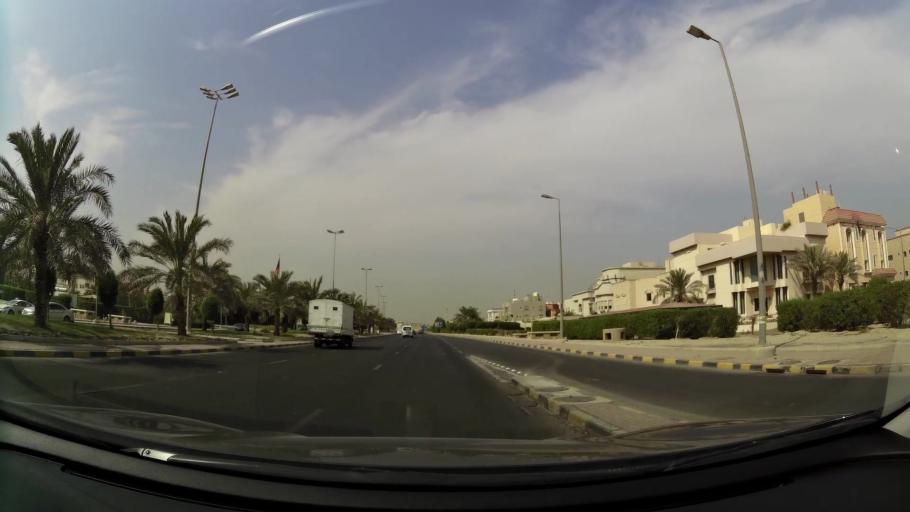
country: KW
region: Al Farwaniyah
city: Janub as Surrah
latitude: 29.2826
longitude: 48.0098
